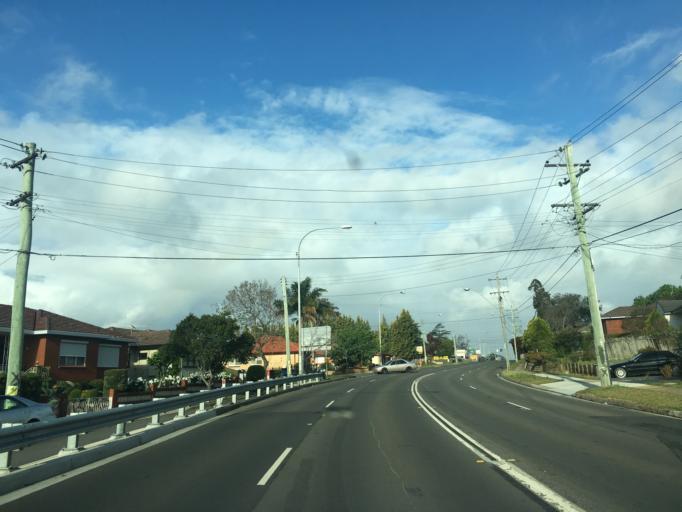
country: AU
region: New South Wales
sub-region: Fairfield
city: Fairfield Heights
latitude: -33.8505
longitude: 150.9192
